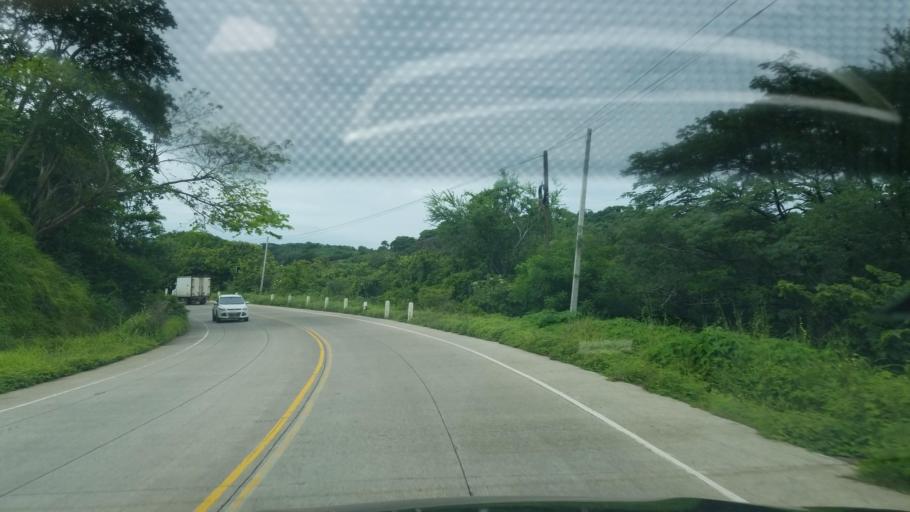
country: HN
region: Choluteca
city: Pespire
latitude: 13.6231
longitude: -87.3742
